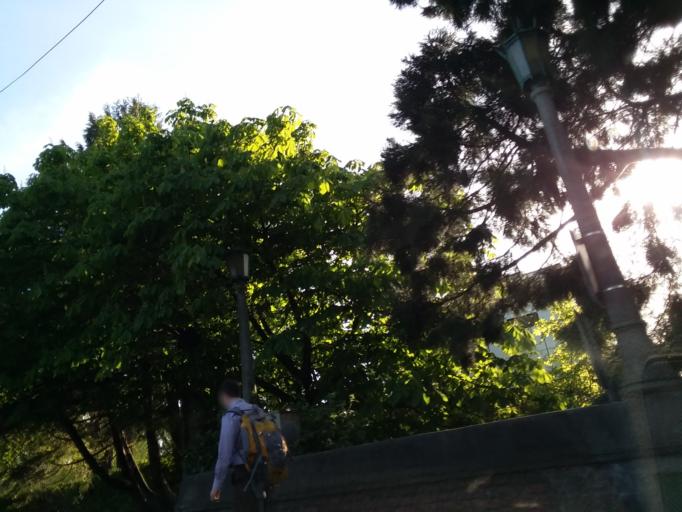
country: US
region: Washington
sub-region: King County
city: Seattle
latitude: 47.6468
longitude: -122.3047
